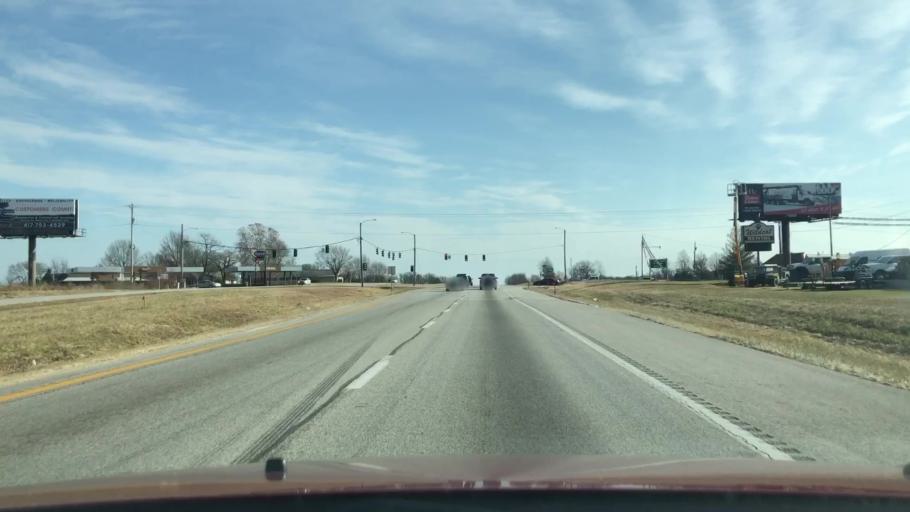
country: US
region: Missouri
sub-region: Webster County
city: Rogersville
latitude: 37.1187
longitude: -93.1211
